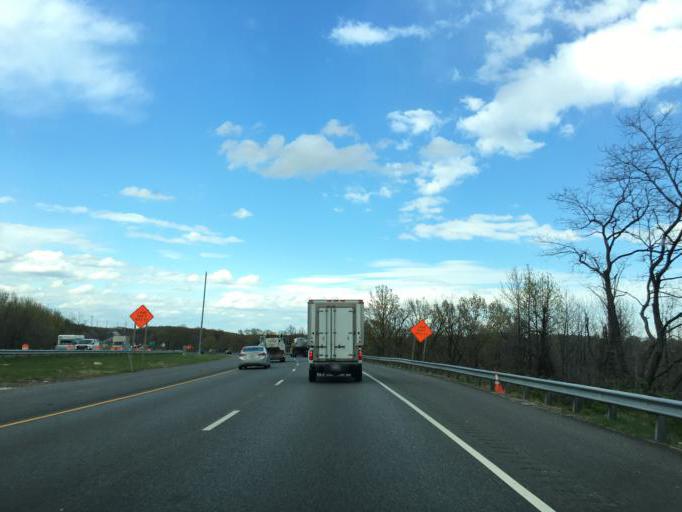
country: US
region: Maryland
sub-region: Baltimore County
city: Essex
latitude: 39.3144
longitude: -76.4921
